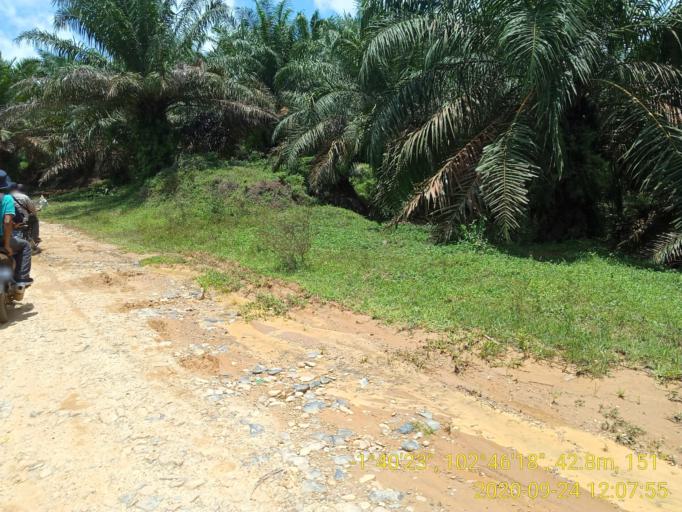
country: ID
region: Jambi
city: Sungaibengkal
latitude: -1.6731
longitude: 102.7716
